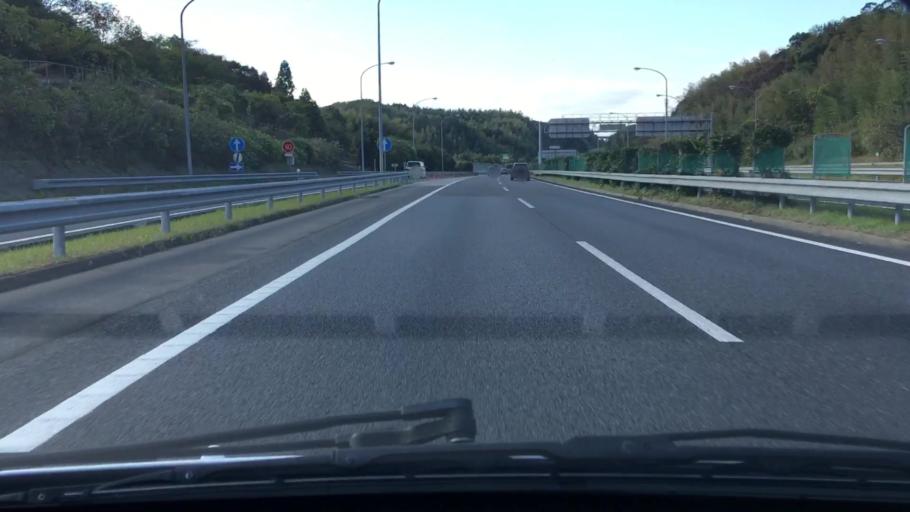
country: JP
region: Chiba
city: Kisarazu
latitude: 35.3733
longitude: 139.9761
